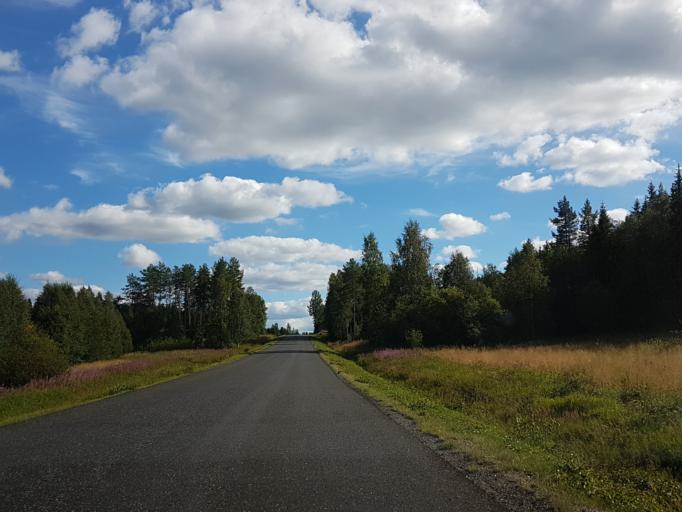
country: SE
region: Vaesterbotten
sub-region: Skelleftea Kommun
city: Burtraesk
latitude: 64.2904
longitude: 20.5241
